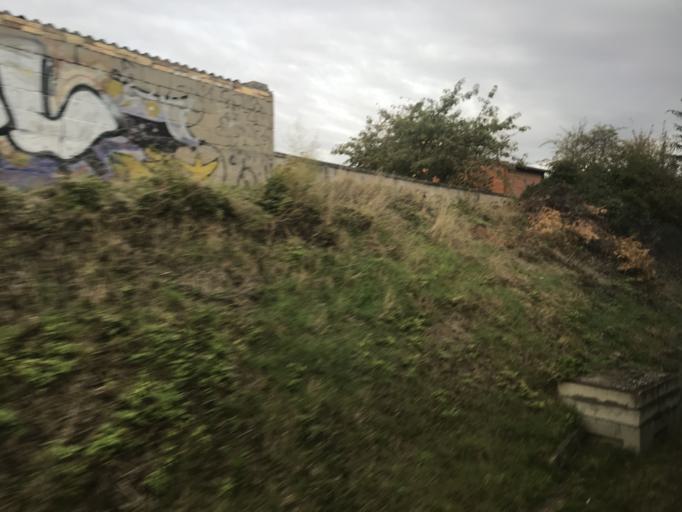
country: DE
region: Rheinland-Pfalz
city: Armsheim
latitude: 49.8095
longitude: 8.0730
